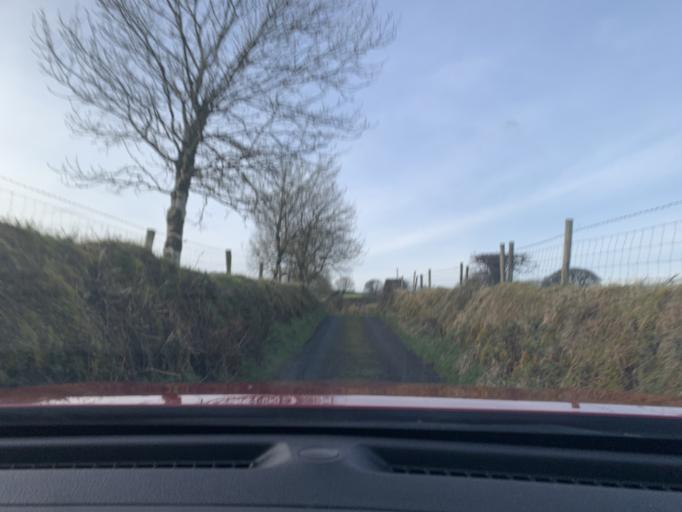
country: IE
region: Connaught
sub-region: Sligo
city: Strandhill
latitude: 54.1713
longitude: -8.6576
